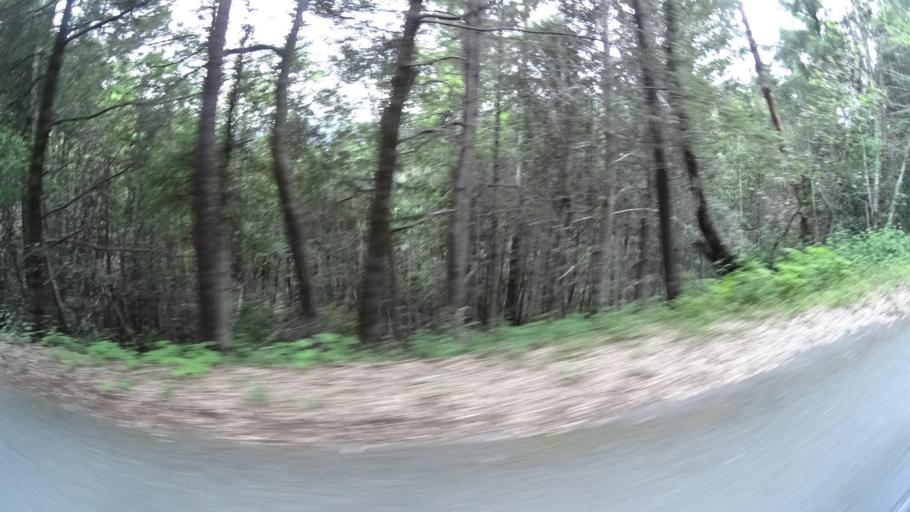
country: US
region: California
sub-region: Humboldt County
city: Willow Creek
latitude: 41.1979
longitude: -123.7570
